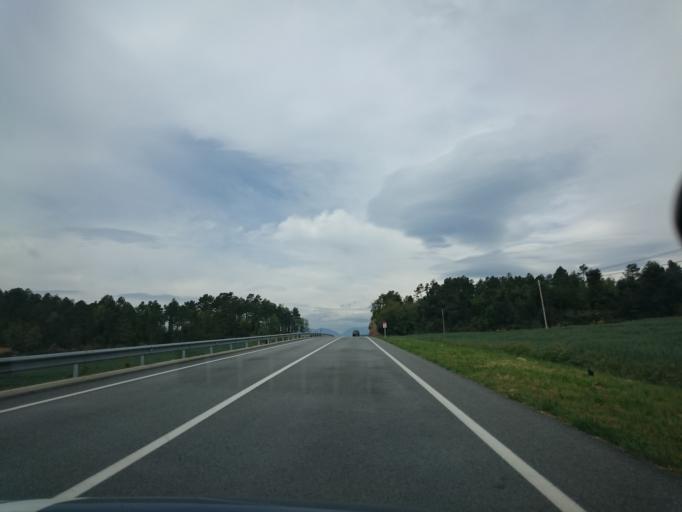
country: ES
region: Catalonia
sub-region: Provincia de Barcelona
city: Olost
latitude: 42.0090
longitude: 2.0848
